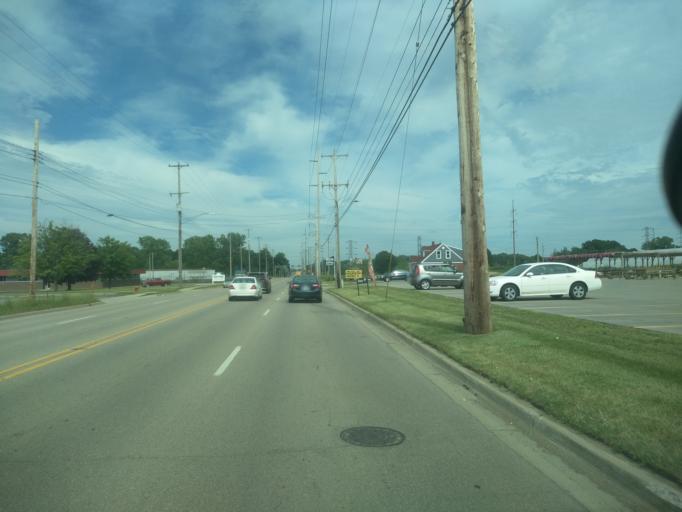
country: US
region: Michigan
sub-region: Ingham County
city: Holt
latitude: 42.6829
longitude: -84.5334
